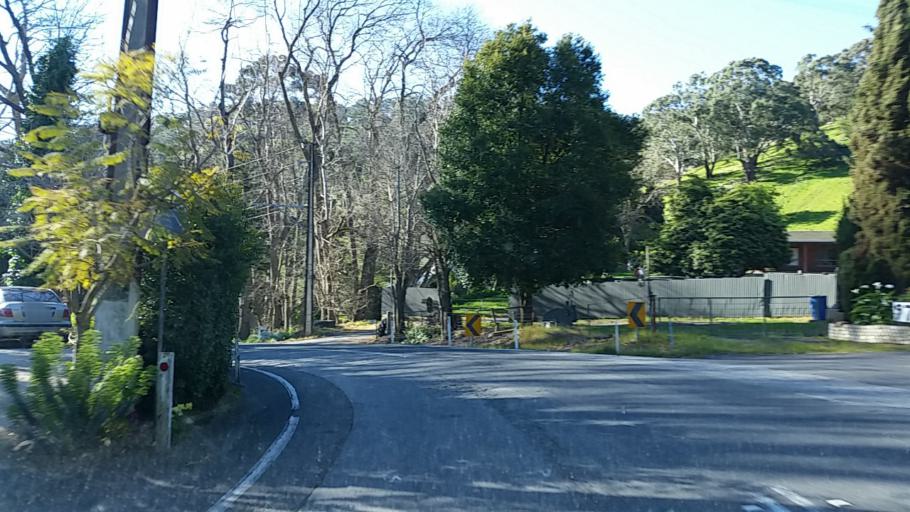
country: AU
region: South Australia
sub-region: Adelaide Hills
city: Adelaide Hills
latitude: -34.9226
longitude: 138.7184
